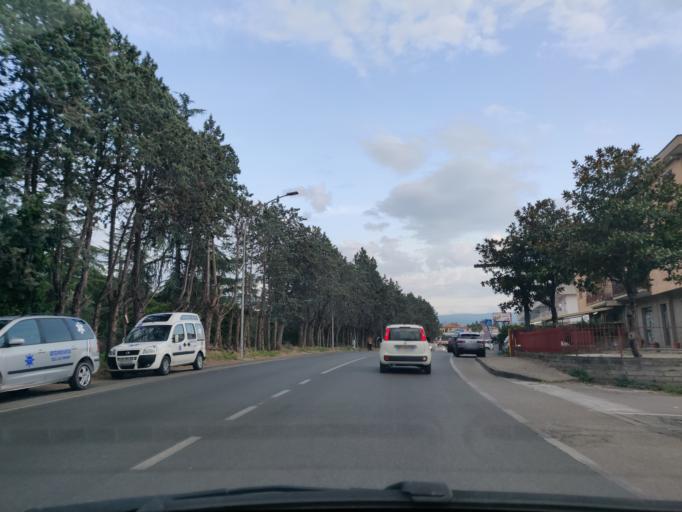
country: IT
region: Latium
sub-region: Provincia di Viterbo
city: Viterbo
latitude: 42.4358
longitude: 12.0975
